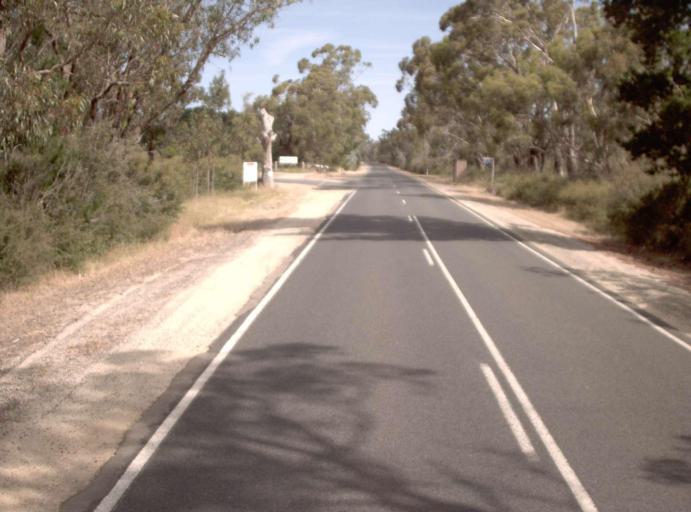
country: AU
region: Victoria
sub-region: Wellington
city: Sale
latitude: -38.2401
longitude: 147.1285
